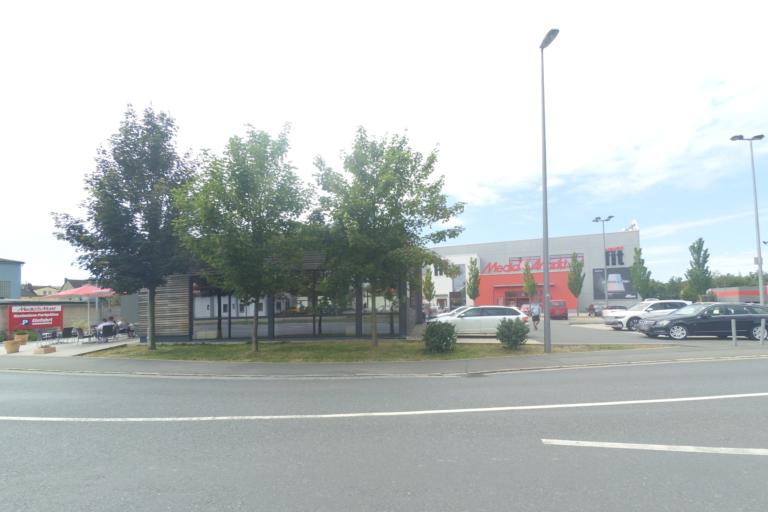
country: DE
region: Bavaria
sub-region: Upper Franconia
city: Kulmbach
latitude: 50.1124
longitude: 11.4476
